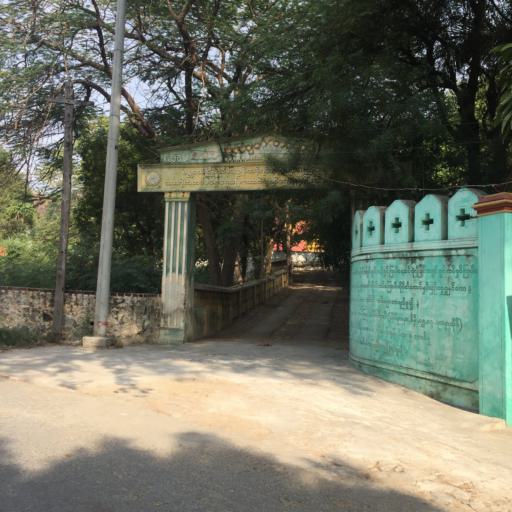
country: MM
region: Sagain
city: Sagaing
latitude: 21.9004
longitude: 95.9967
